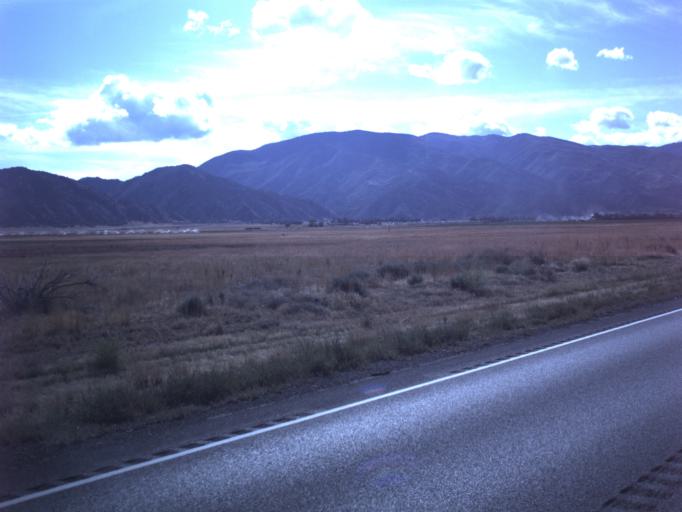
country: US
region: Utah
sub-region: Juab County
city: Nephi
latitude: 39.5844
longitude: -111.8618
